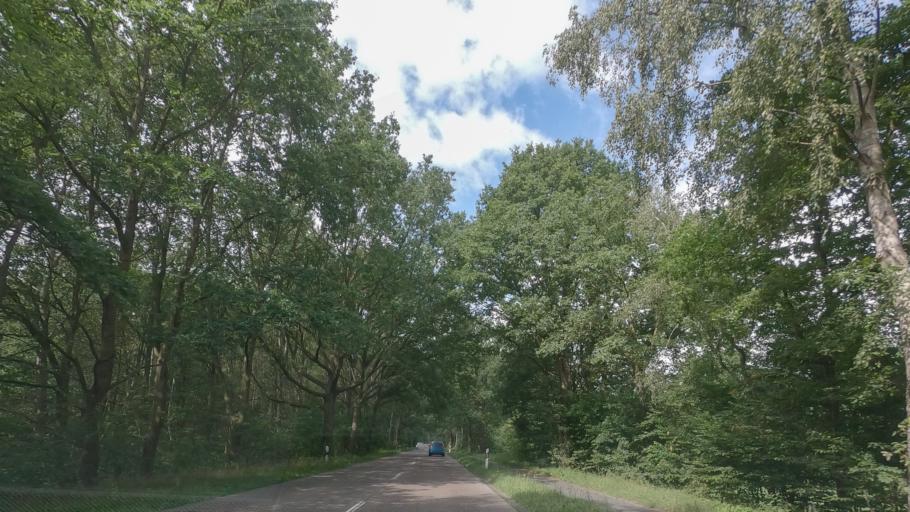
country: DE
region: Lower Saxony
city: Schwanewede
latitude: 53.2313
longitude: 8.5773
